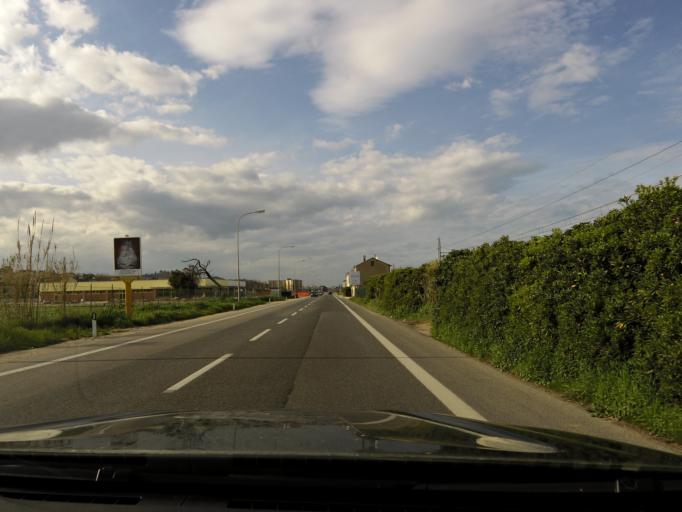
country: IT
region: The Marches
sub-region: Provincia di Macerata
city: Porto Potenza Picena
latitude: 43.3400
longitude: 13.7074
